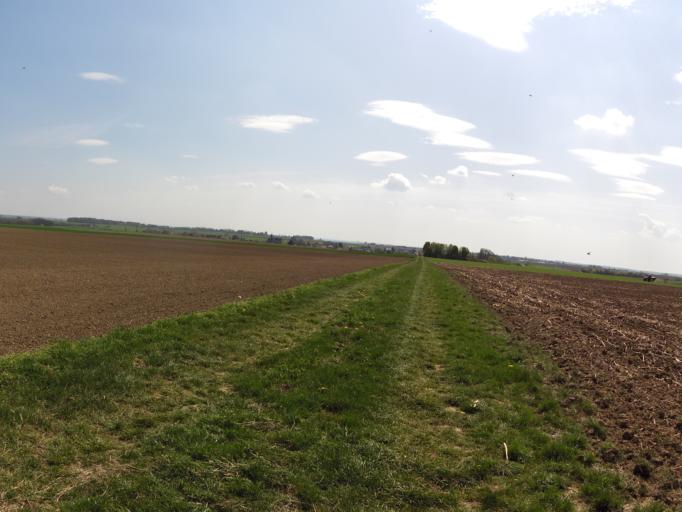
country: DE
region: Bavaria
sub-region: Regierungsbezirk Unterfranken
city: Giebelstadt
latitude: 49.6811
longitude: 9.9560
